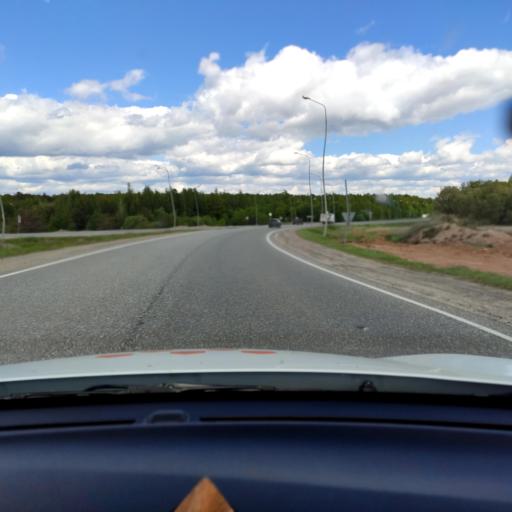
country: RU
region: Tatarstan
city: Sviyazhsk
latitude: 55.7388
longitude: 48.7867
